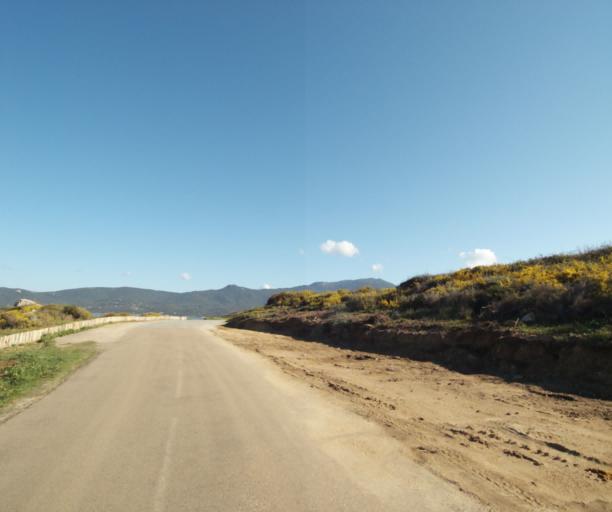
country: FR
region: Corsica
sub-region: Departement de la Corse-du-Sud
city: Propriano
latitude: 41.6655
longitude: 8.8825
